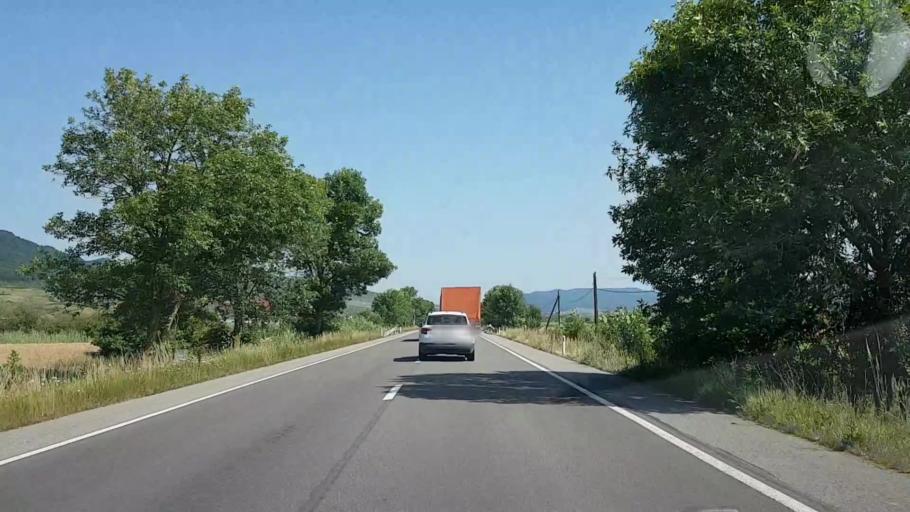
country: RO
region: Bistrita-Nasaud
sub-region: Comuna Sieu-Magherus
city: Sieu-Magherus
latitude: 47.1060
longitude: 24.3519
